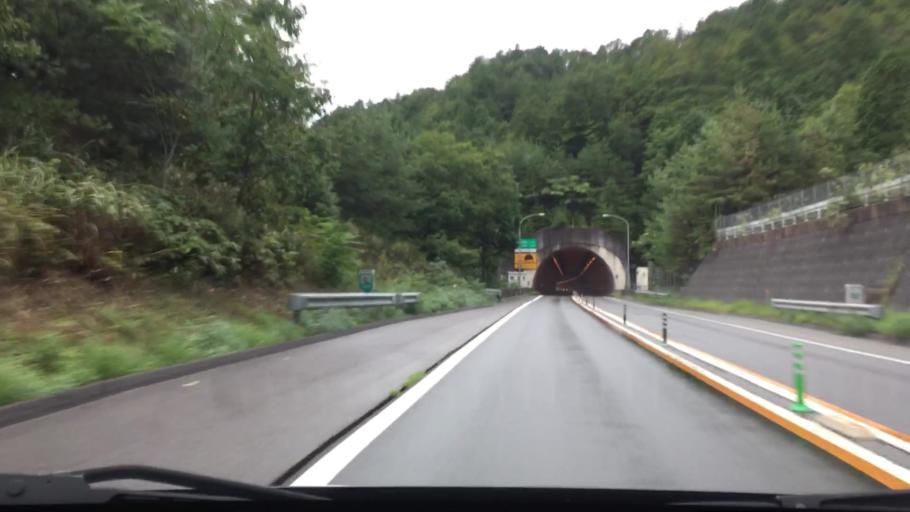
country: JP
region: Hyogo
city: Toyooka
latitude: 35.2759
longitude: 134.8146
